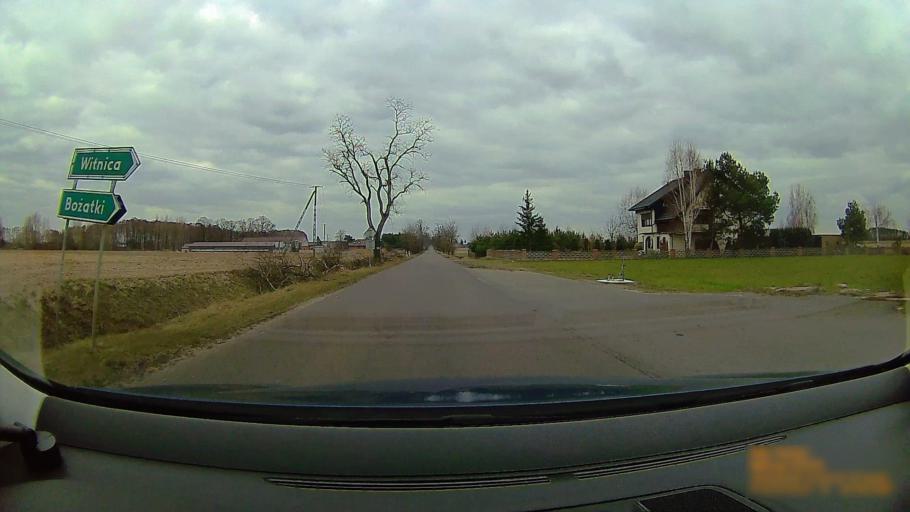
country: PL
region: Greater Poland Voivodeship
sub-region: Powiat koninski
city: Rzgow Pierwszy
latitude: 52.1289
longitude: 18.0503
